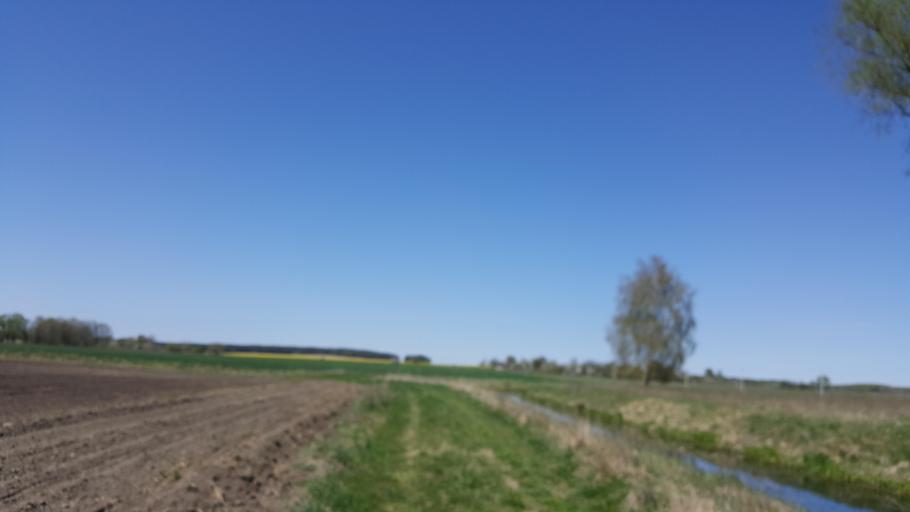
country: BY
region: Brest
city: Charnawchytsy
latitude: 52.3171
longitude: 23.7138
